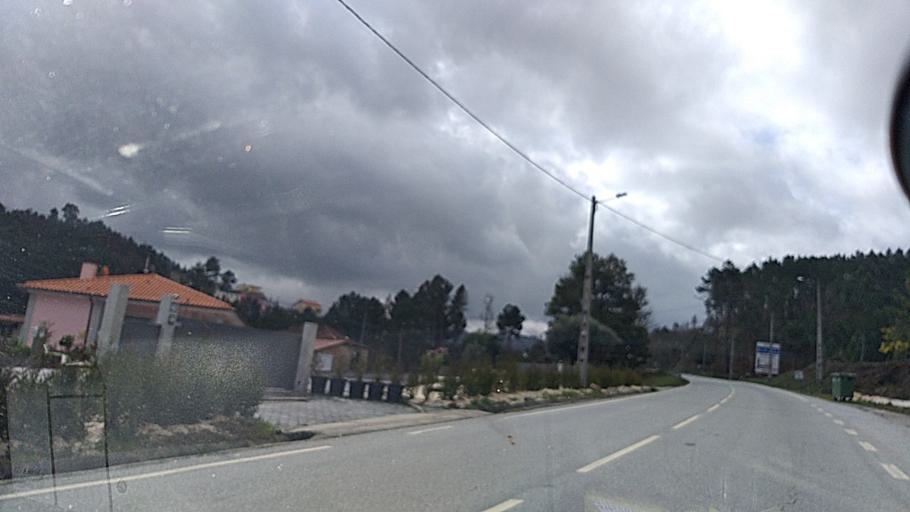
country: PT
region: Viseu
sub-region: Mangualde
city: Mangualde
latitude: 40.6414
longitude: -7.7387
